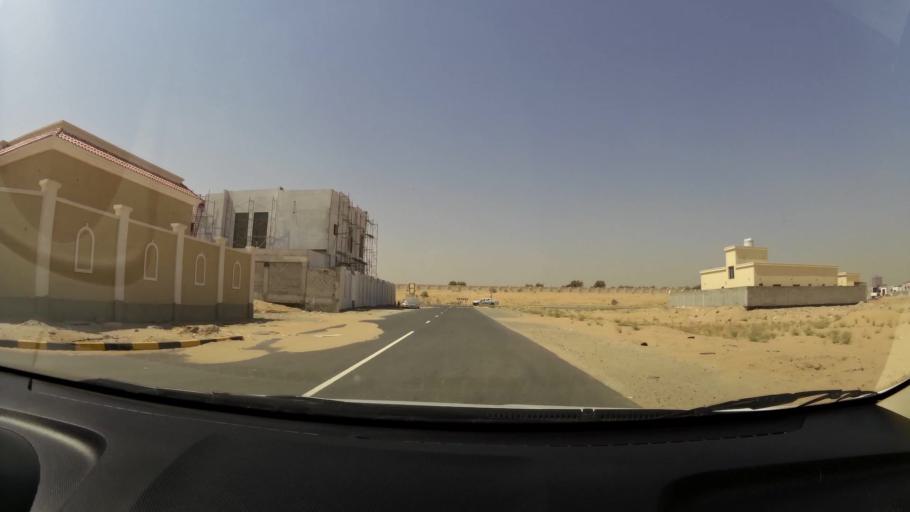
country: AE
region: Ajman
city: Ajman
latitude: 25.4047
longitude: 55.5306
